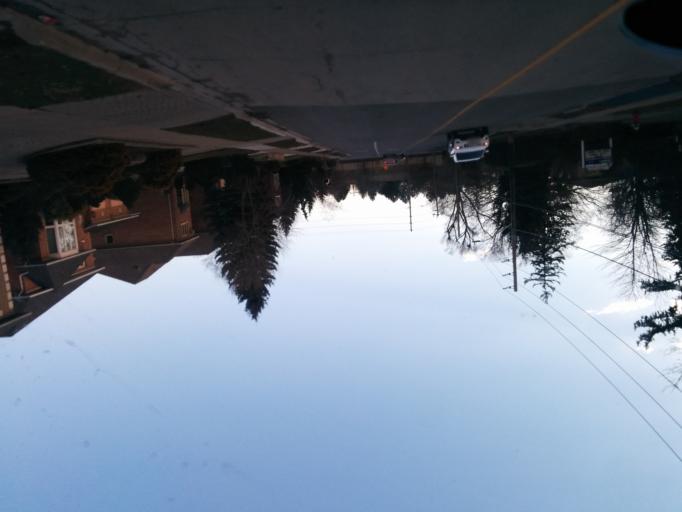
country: CA
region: Ontario
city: Mississauga
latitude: 43.5356
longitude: -79.6329
